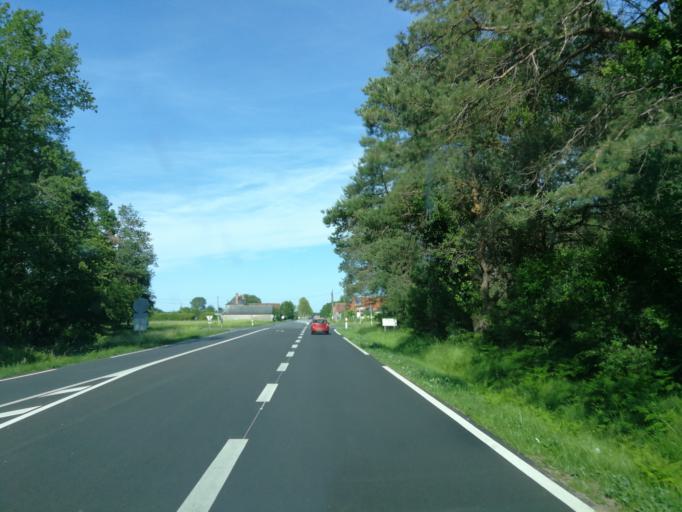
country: FR
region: Centre
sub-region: Departement d'Indre-et-Loire
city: Sache
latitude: 47.2925
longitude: 0.5333
